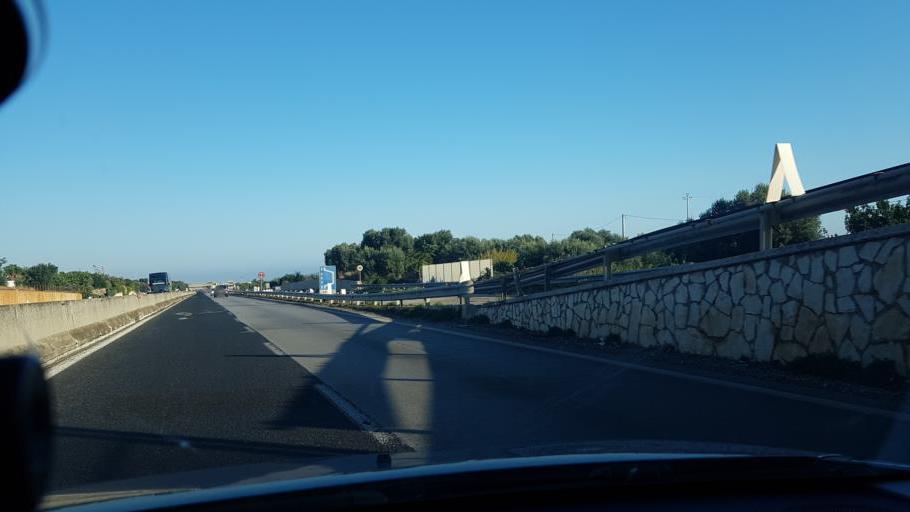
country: IT
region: Apulia
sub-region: Provincia di Brindisi
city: Fasano
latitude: 40.8849
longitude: 17.3359
